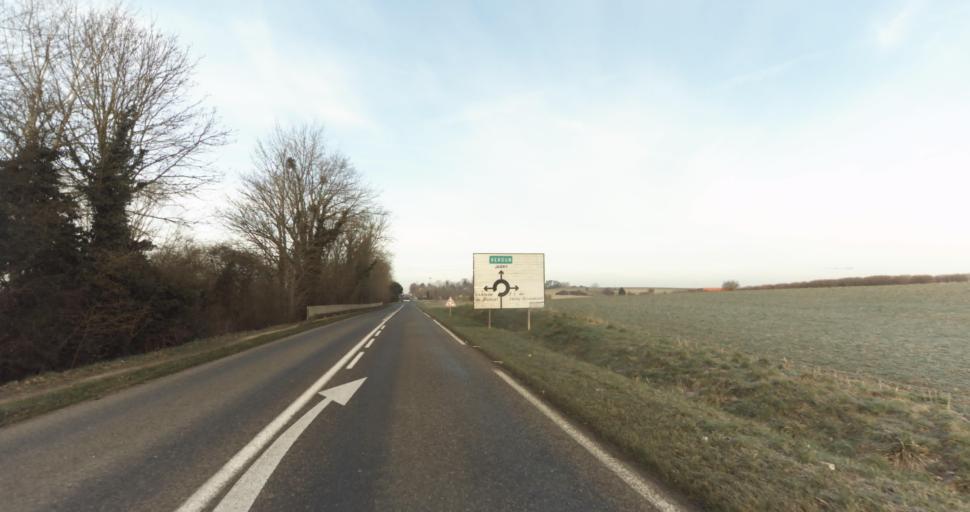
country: FR
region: Lorraine
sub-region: Departement de Meurthe-et-Moselle
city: Giraumont
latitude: 49.1507
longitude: 5.9064
